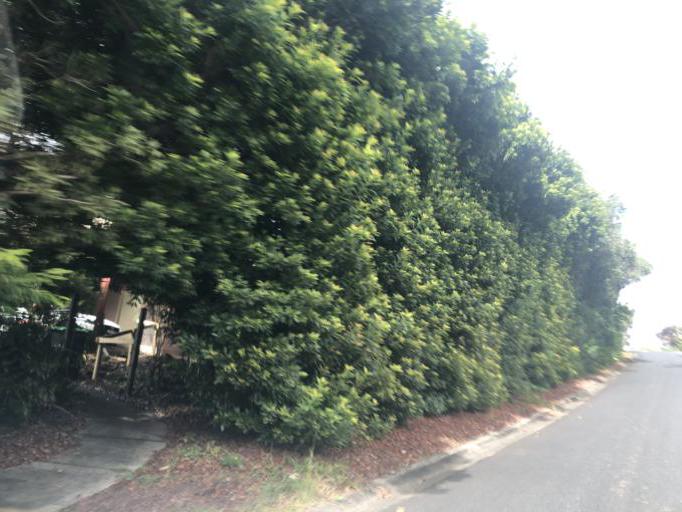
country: AU
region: New South Wales
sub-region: Bellingen
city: Bellingen
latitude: -30.4463
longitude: 152.9042
